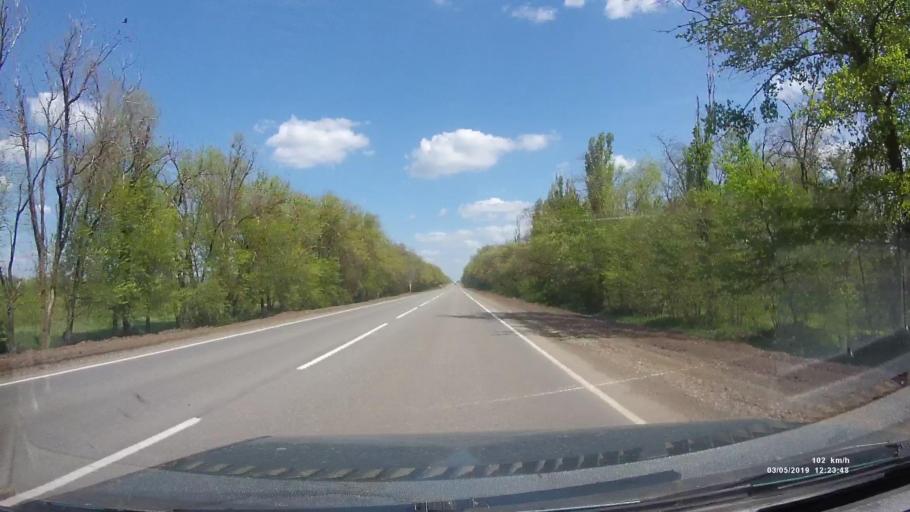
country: RU
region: Rostov
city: Semikarakorsk
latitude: 47.4131
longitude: 40.6891
